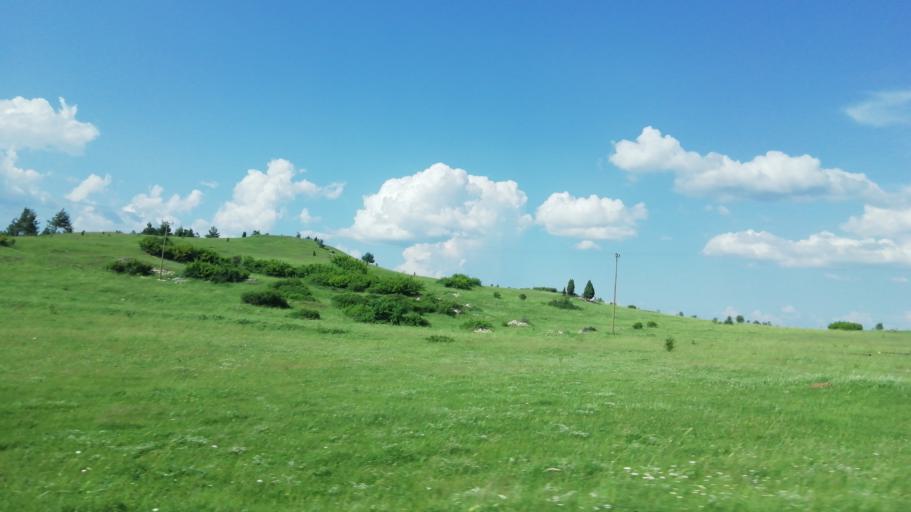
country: TR
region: Karabuk
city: Karabuk
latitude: 41.1307
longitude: 32.5732
